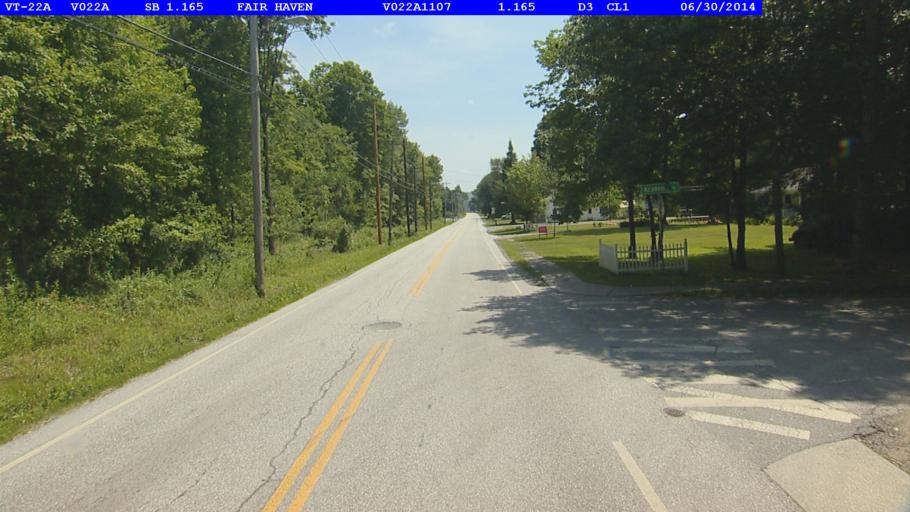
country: US
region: Vermont
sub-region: Rutland County
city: Fair Haven
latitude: 43.5848
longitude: -73.2650
